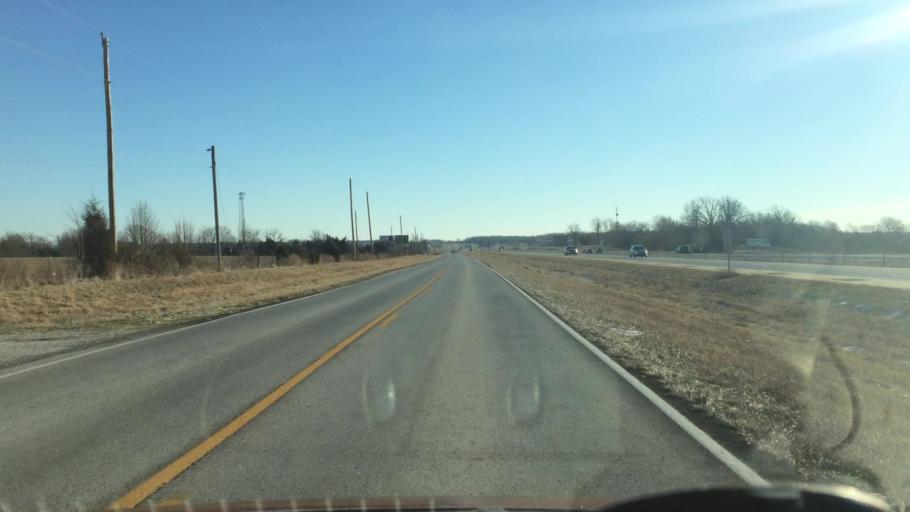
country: US
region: Missouri
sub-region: Greene County
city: Strafford
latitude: 37.2709
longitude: -93.0953
